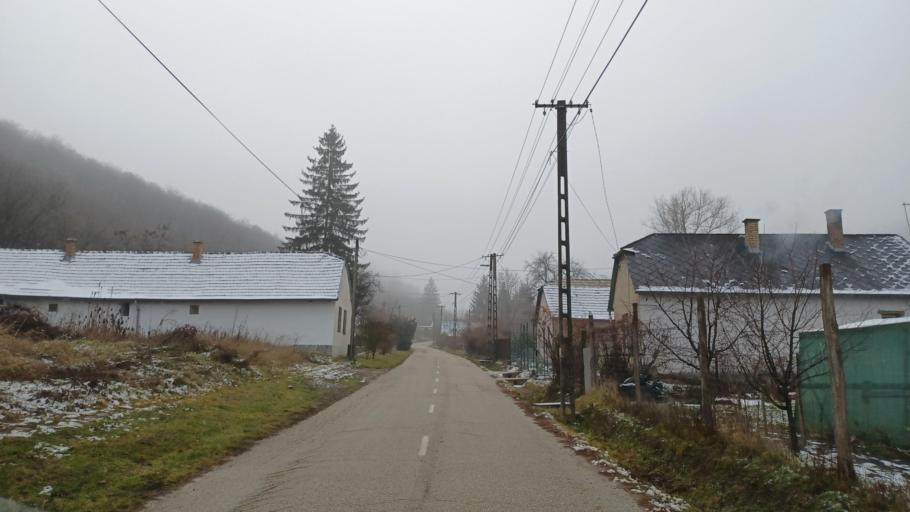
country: HU
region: Tolna
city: Pincehely
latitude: 46.6282
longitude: 18.4784
